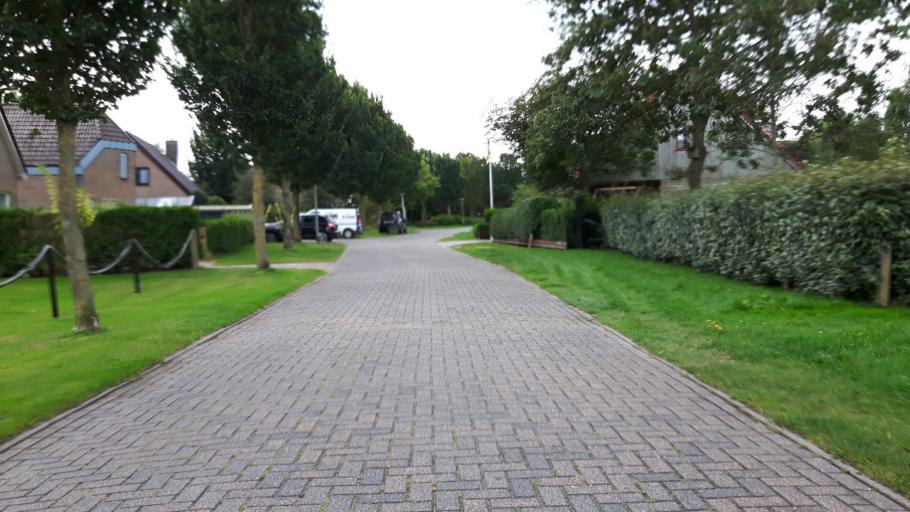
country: NL
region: Friesland
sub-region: Gemeente Ameland
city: Hollum
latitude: 53.4457
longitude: 5.6897
